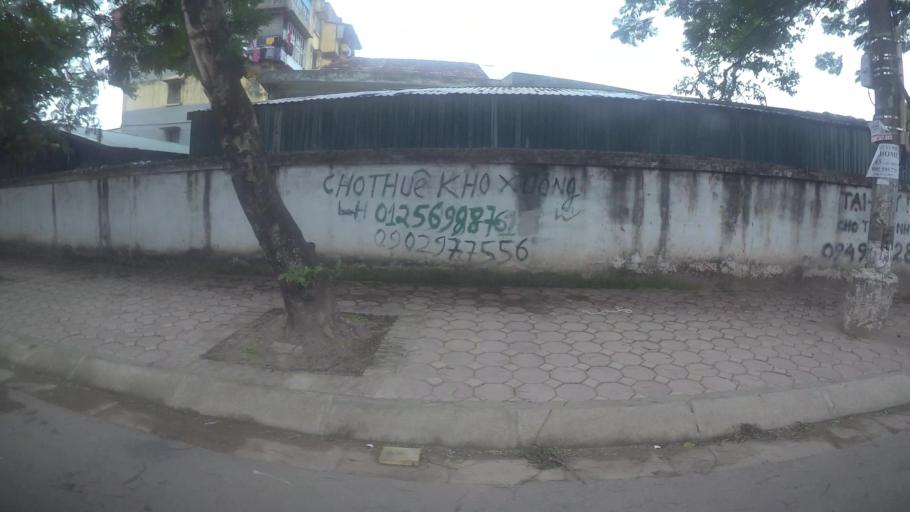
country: VN
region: Ha Noi
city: Tay Ho
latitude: 21.0874
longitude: 105.7913
